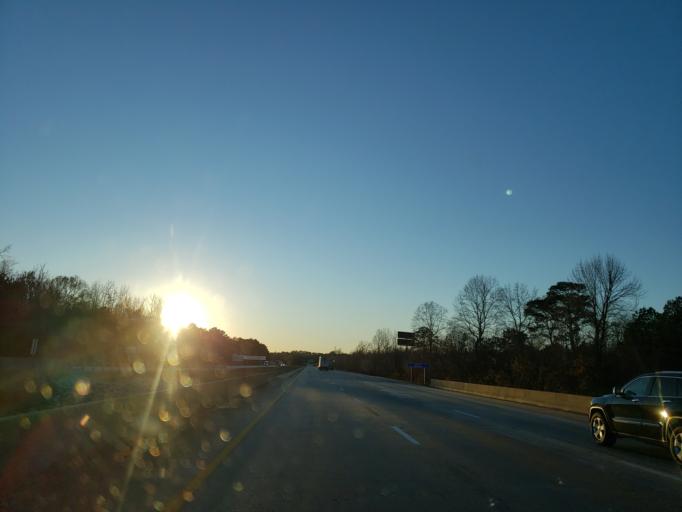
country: US
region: Mississippi
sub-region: Lauderdale County
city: Meridian
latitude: 32.3485
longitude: -88.7550
